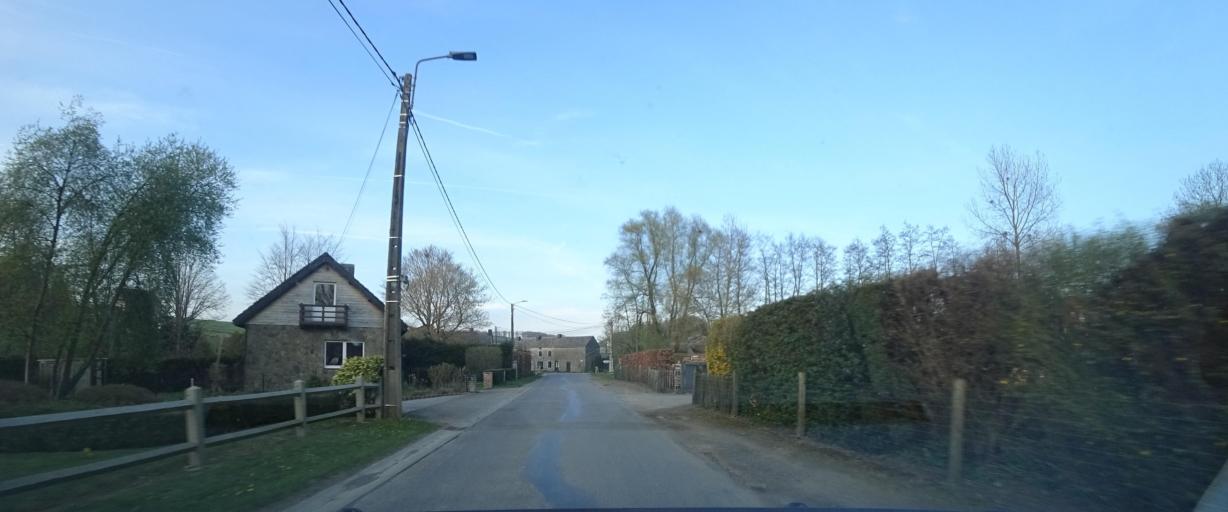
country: BE
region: Wallonia
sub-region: Province de Namur
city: Hamois
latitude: 50.3179
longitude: 5.1912
